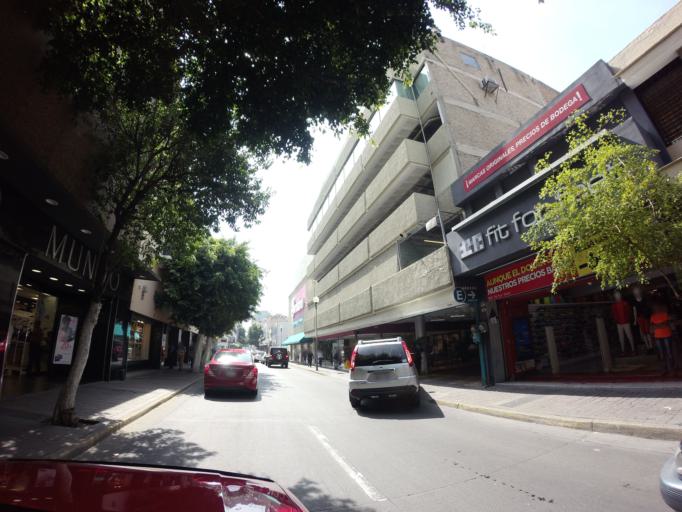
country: MX
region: Jalisco
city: Guadalajara
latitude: 20.6743
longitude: -103.3502
